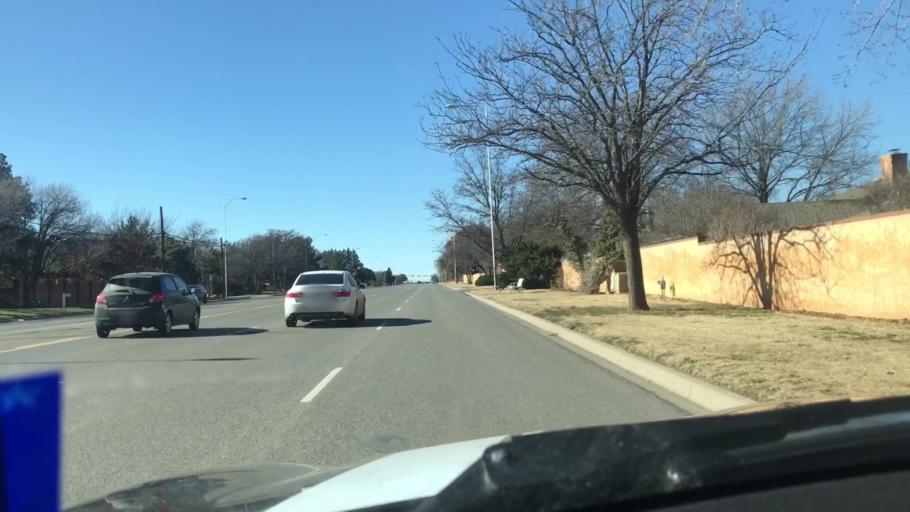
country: US
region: Texas
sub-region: Lubbock County
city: Lubbock
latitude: 33.5779
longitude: -101.9253
